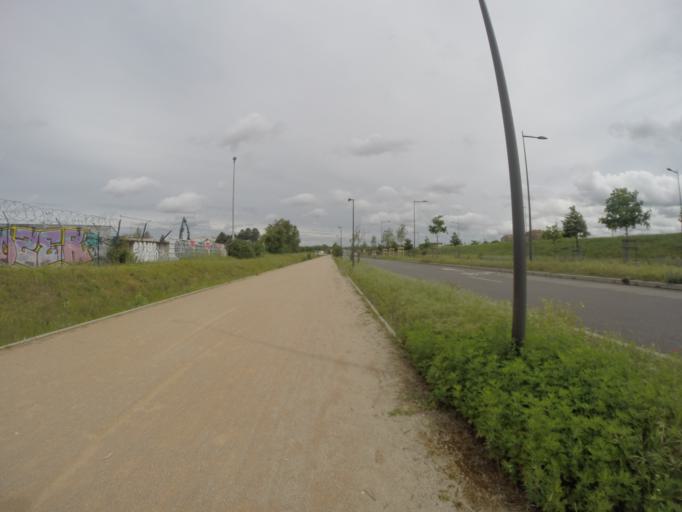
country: FR
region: Rhone-Alpes
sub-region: Departement du Rhone
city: Vaulx-en-Velin
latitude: 45.7653
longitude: 4.9328
